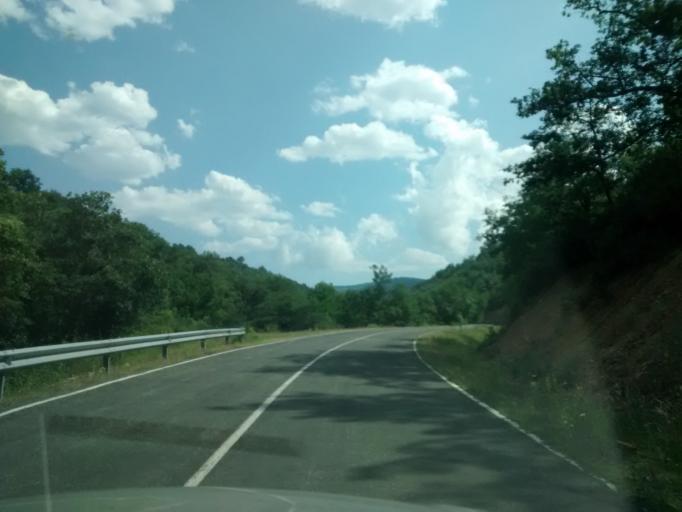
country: ES
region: La Rioja
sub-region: Provincia de La Rioja
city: Rabanera
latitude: 42.1805
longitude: -2.4839
